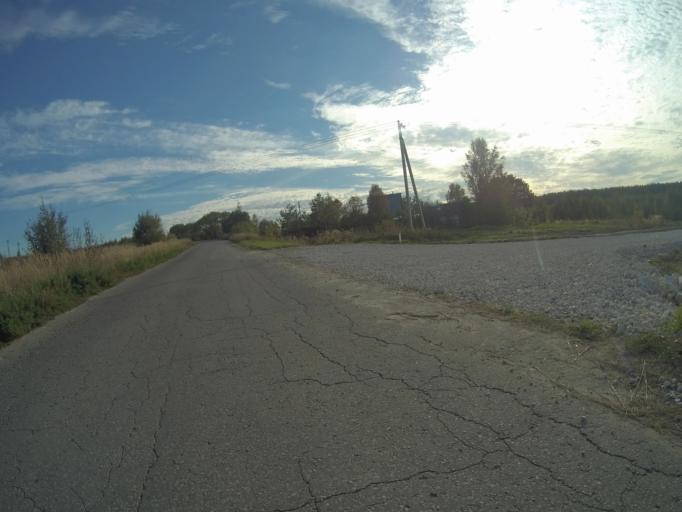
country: RU
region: Vladimir
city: Golovino
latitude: 55.9655
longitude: 40.4551
